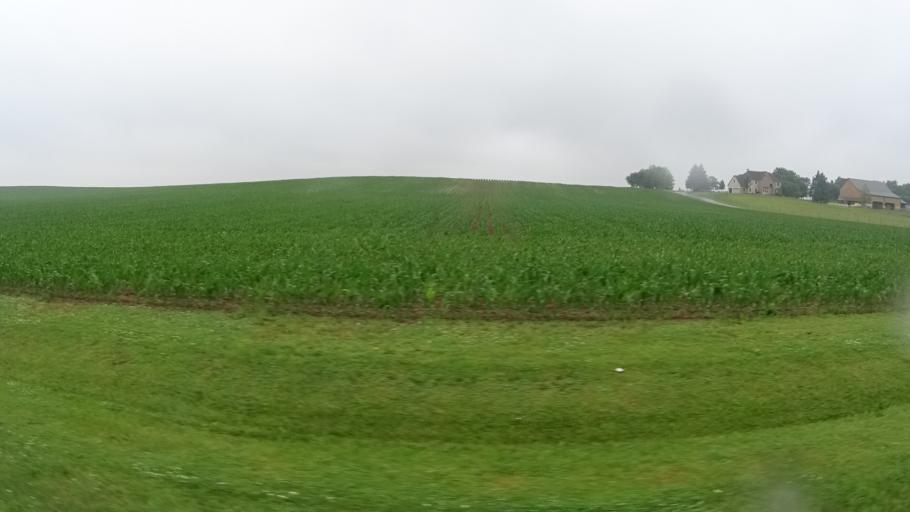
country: US
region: Ohio
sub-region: Huron County
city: Bellevue
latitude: 41.3337
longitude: -82.8433
